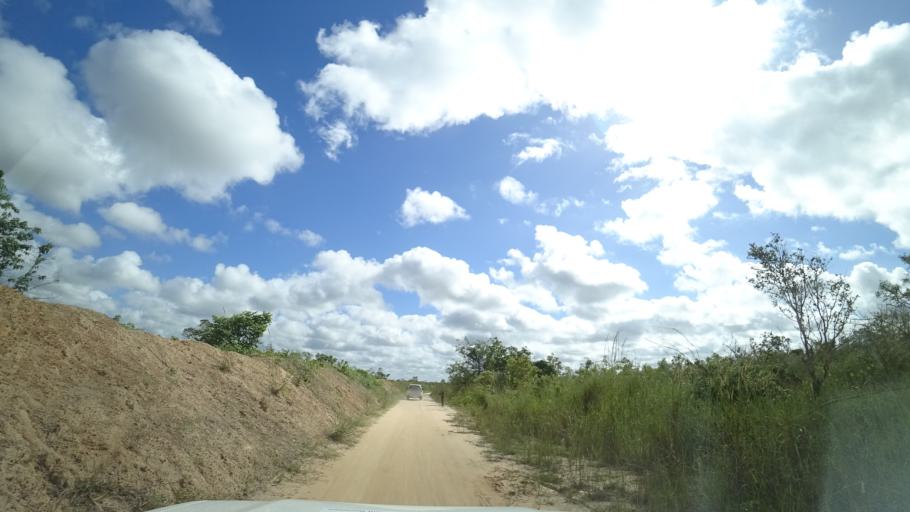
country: MZ
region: Sofala
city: Beira
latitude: -19.6191
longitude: 35.0605
